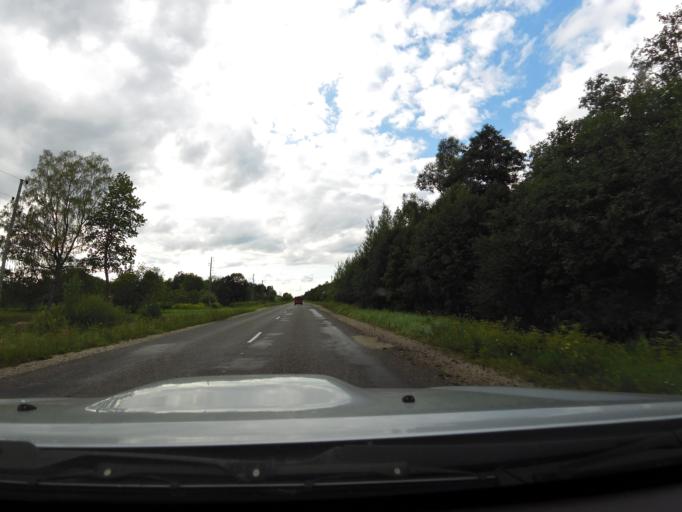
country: LV
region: Akniste
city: Akniste
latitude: 55.9937
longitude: 25.9719
